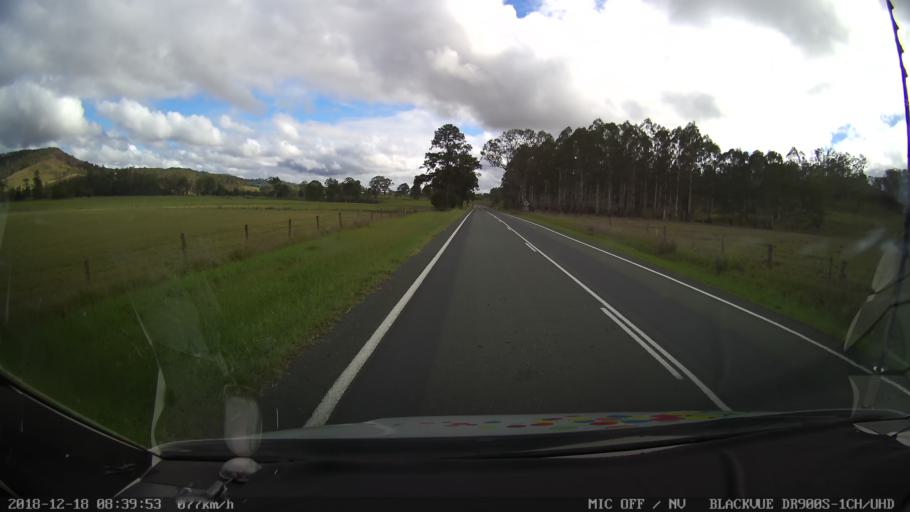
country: AU
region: Queensland
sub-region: Logan
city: Cedar Vale
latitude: -28.2476
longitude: 152.8431
